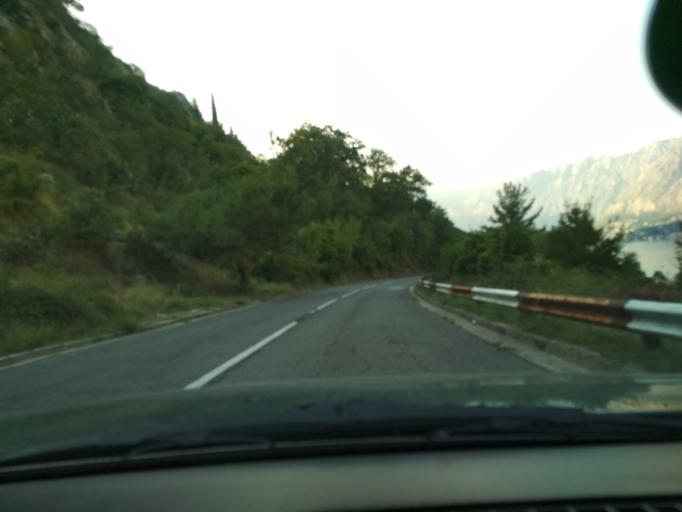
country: ME
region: Kotor
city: Kotor
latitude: 42.4194
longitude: 18.7587
